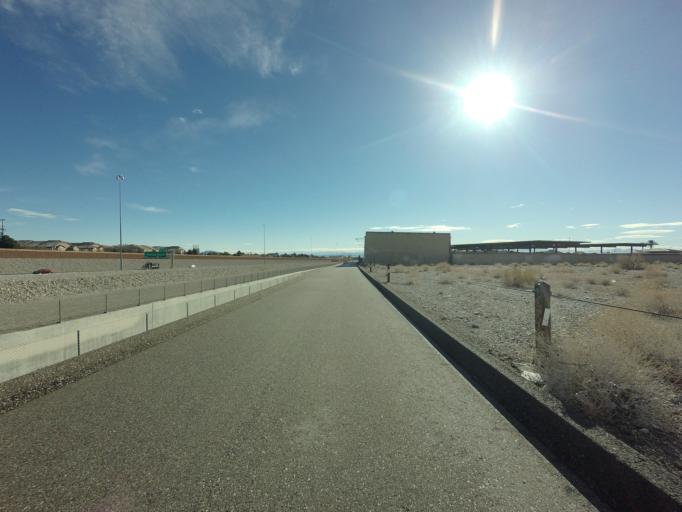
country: US
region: Nevada
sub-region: Clark County
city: Summerlin South
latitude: 36.1176
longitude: -115.3110
